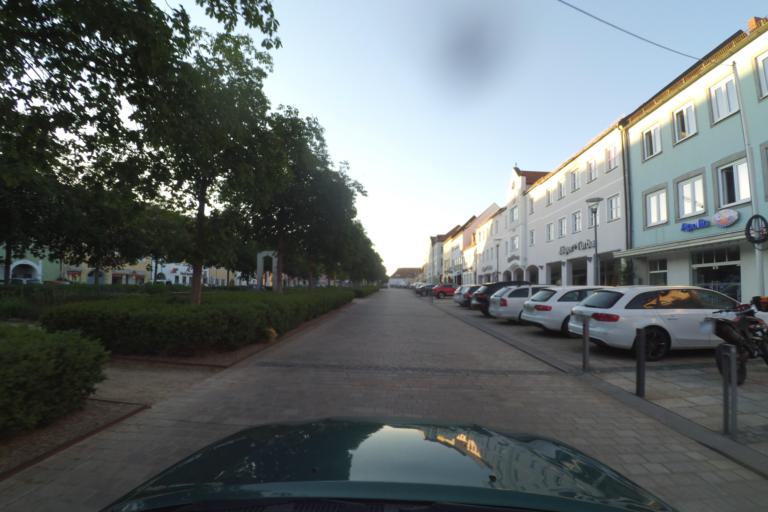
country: DE
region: Bavaria
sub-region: Upper Palatinate
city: Tirschenreuth
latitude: 49.8775
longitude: 12.3378
